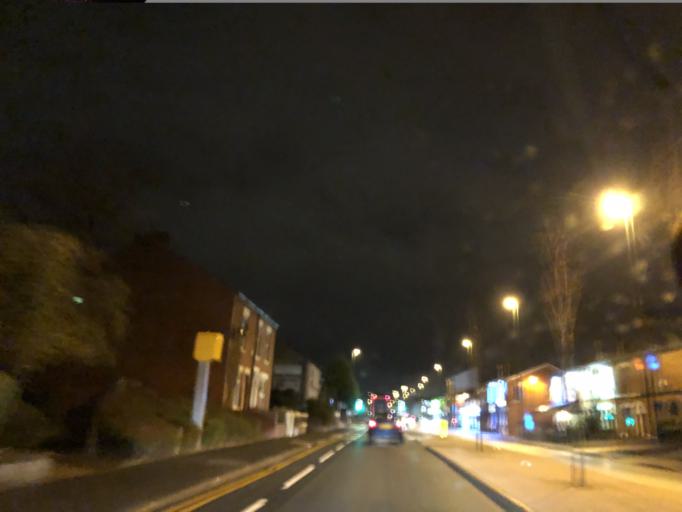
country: GB
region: England
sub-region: Manchester
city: Failsworth
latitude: 53.5143
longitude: -2.1518
